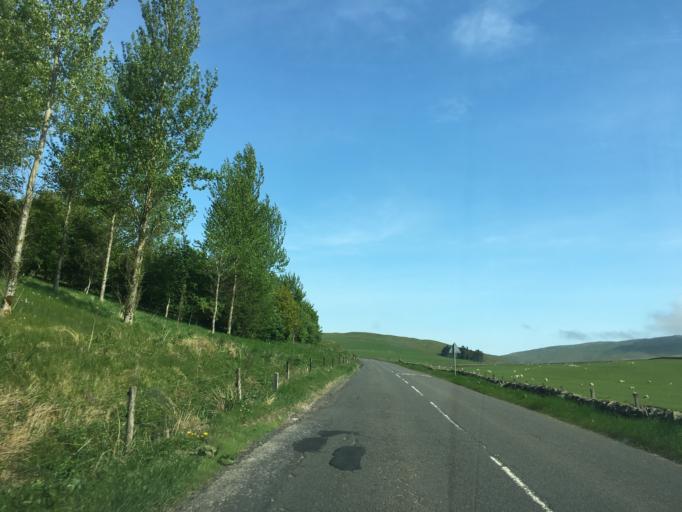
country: GB
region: Scotland
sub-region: South Lanarkshire
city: Biggar
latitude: 55.6374
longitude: -3.4257
